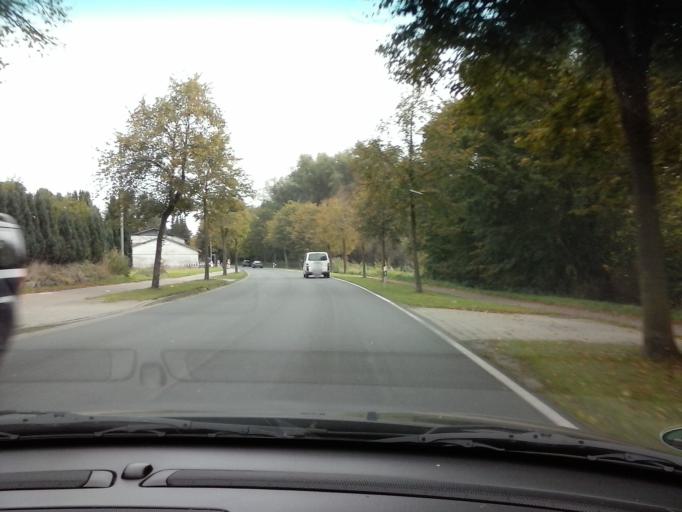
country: DE
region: Lower Saxony
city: Hemmoor
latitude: 53.7052
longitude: 9.1229
